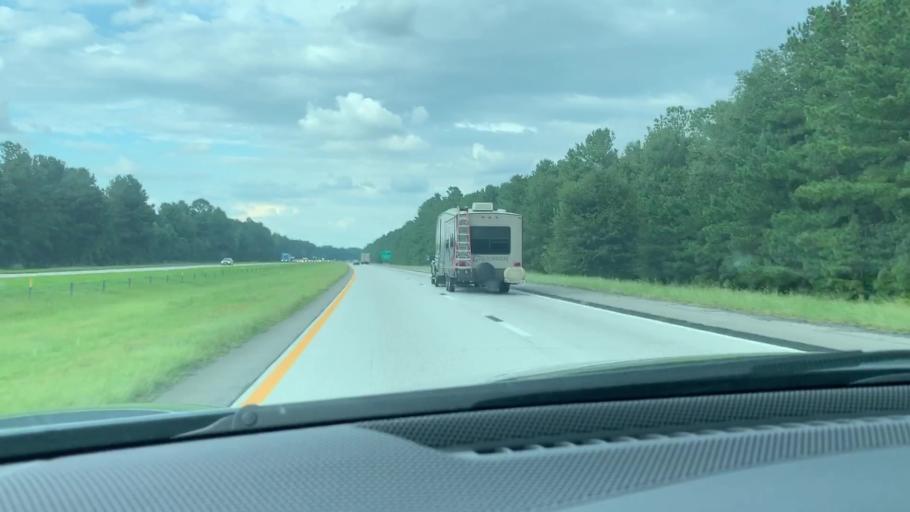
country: US
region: South Carolina
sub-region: Dorchester County
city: Saint George
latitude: 33.2971
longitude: -80.5568
